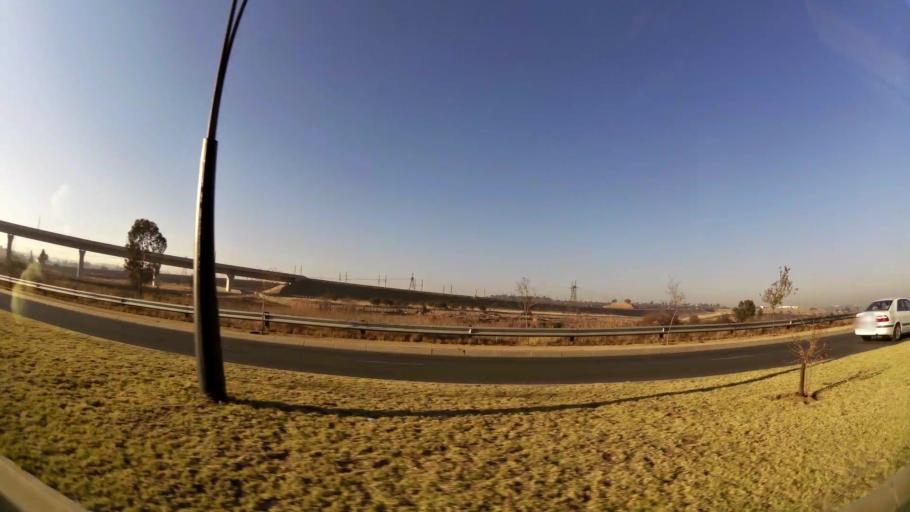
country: ZA
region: Gauteng
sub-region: City of Johannesburg Metropolitan Municipality
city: Midrand
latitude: -26.0269
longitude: 28.1250
